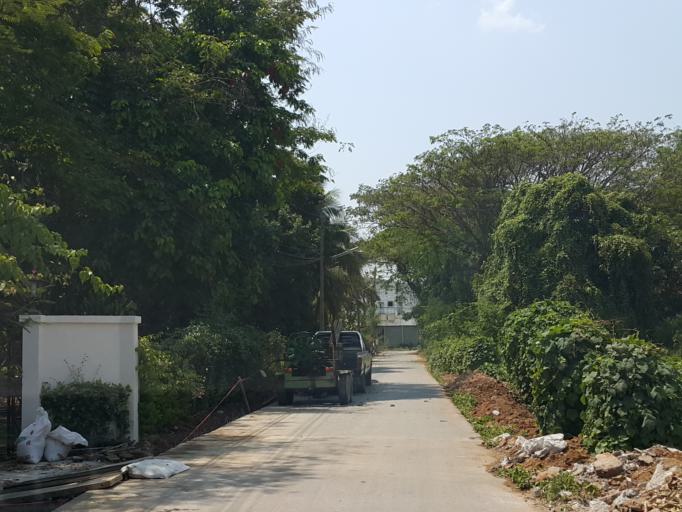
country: TH
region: Chiang Mai
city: Saraphi
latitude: 18.7359
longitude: 98.9924
